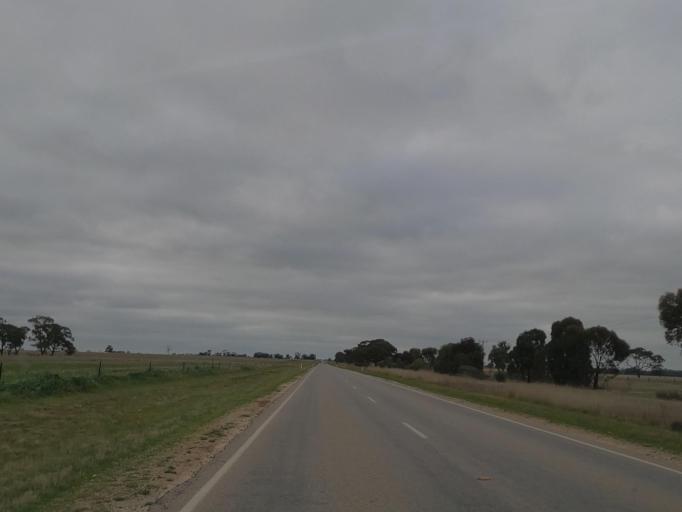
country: AU
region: Victoria
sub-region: Greater Bendigo
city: Long Gully
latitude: -36.5402
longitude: 143.9414
